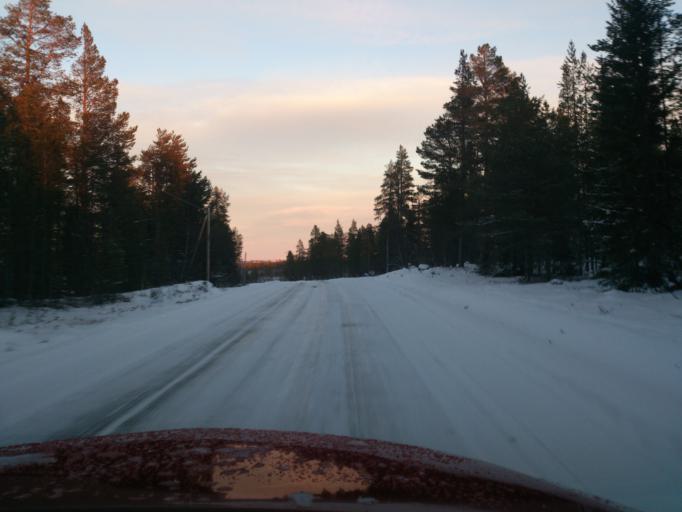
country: SE
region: Jaemtland
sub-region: Harjedalens Kommun
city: Sveg
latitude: 62.3375
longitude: 13.4330
